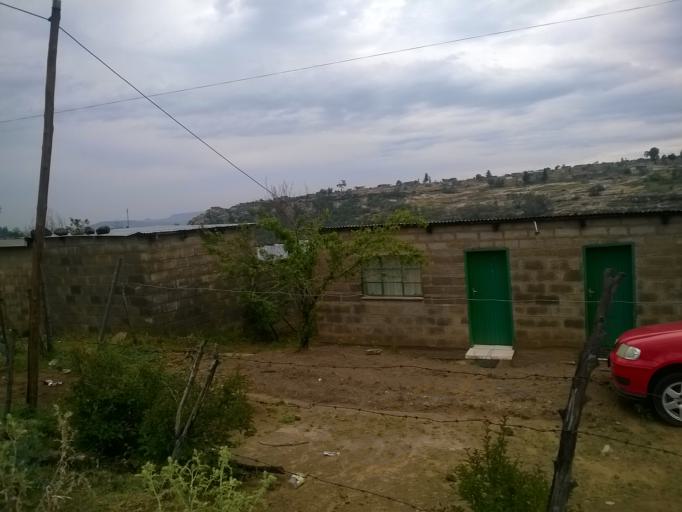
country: LS
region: Berea
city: Teyateyaneng
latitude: -29.1417
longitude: 27.7427
